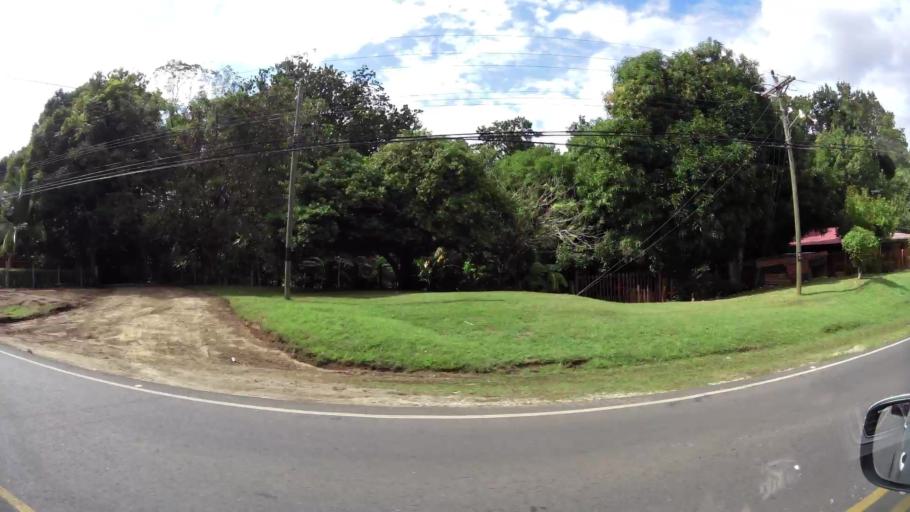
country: CR
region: Guanacaste
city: Hojancha
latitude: 10.1158
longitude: -85.3443
